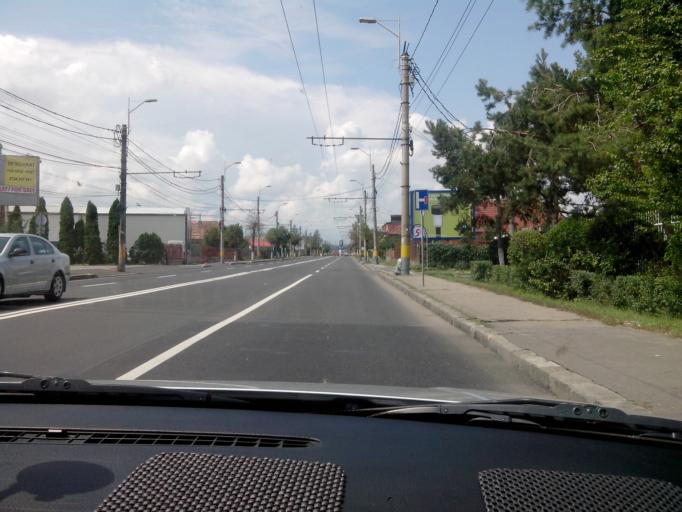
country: RO
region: Cluj
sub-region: Comuna Apahida
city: Sannicoara
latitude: 46.7807
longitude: 23.6751
